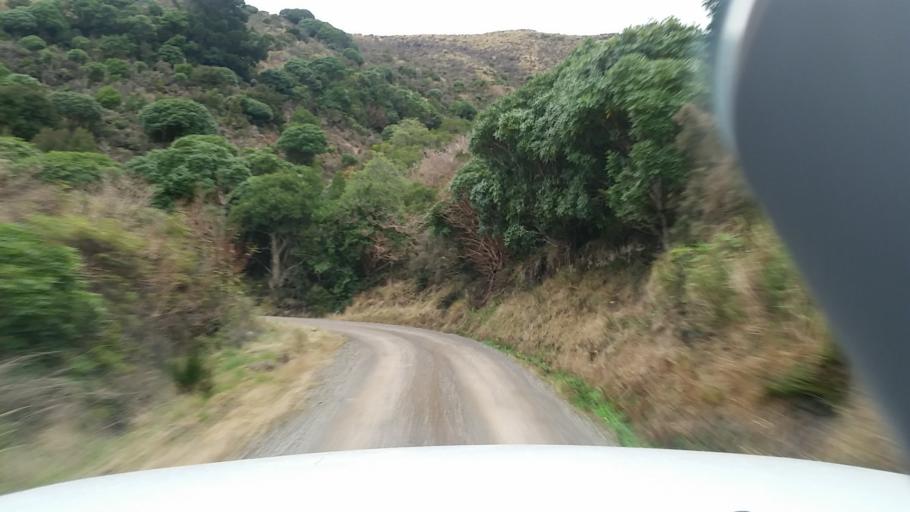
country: NZ
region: Canterbury
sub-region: Christchurch City
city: Christchurch
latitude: -43.8079
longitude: 172.8618
